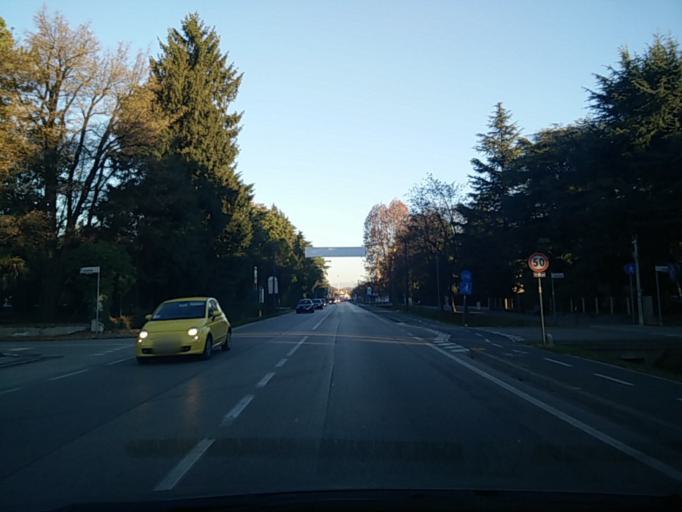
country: IT
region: Veneto
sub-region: Provincia di Treviso
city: Treviso
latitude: 45.6780
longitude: 12.2512
